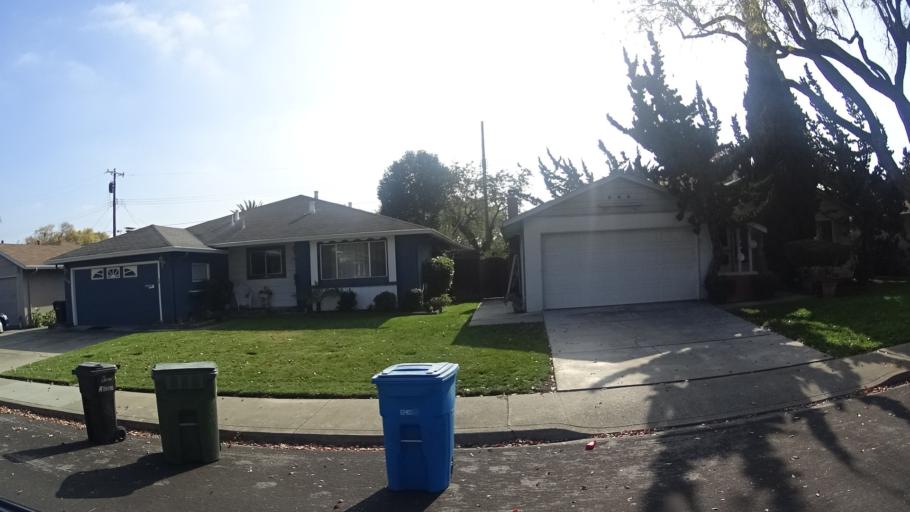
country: US
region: California
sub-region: Santa Clara County
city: Santa Clara
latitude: 37.3626
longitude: -121.9939
